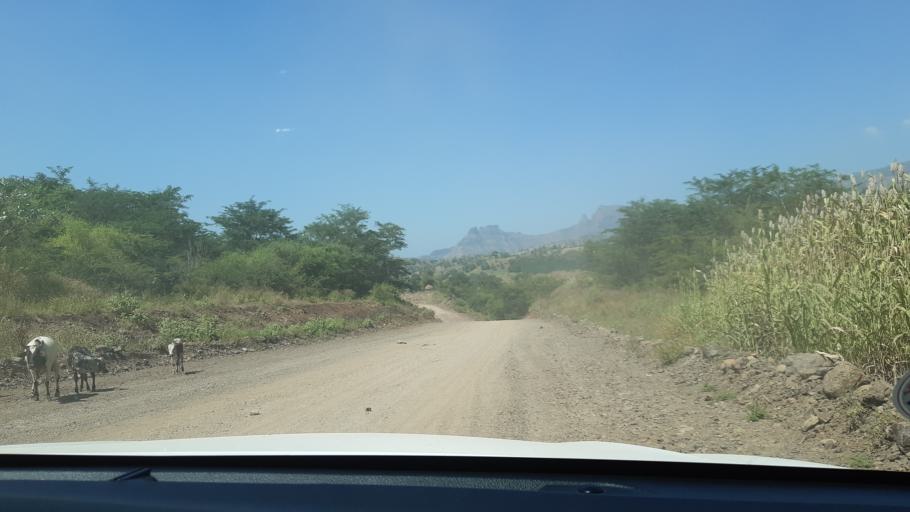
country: ET
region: Amhara
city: Dabat
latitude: 13.1933
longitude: 37.5680
